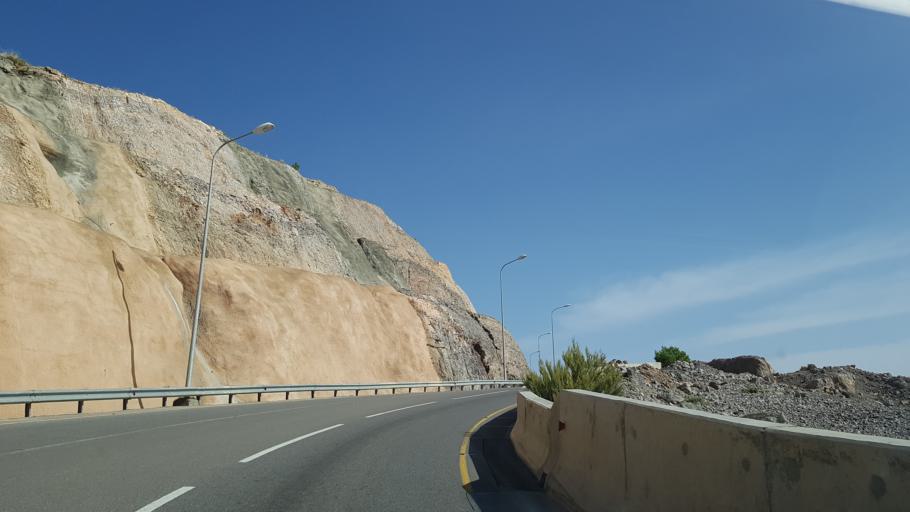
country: OM
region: Muhafazat ad Dakhiliyah
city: Izki
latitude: 23.0608
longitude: 57.7266
